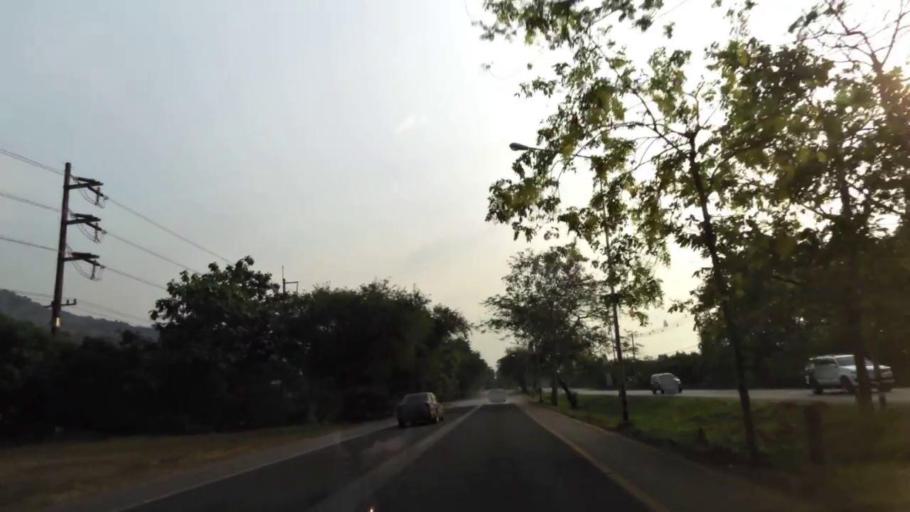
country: TH
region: Chanthaburi
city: Chanthaburi
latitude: 12.5692
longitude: 102.1622
